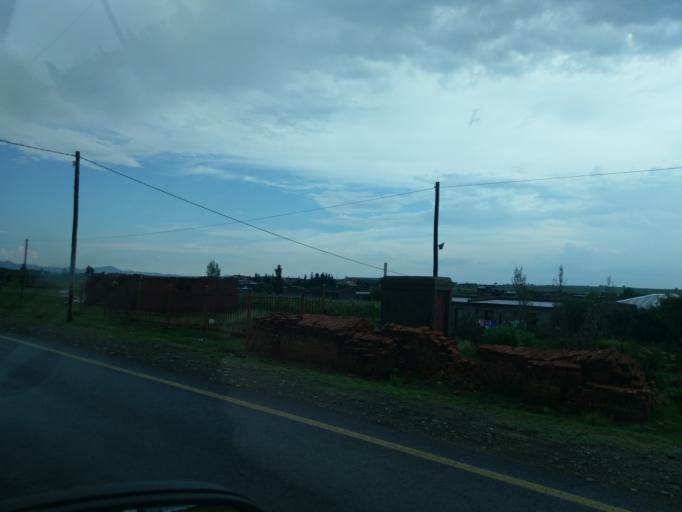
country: LS
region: Mafeteng
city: Mafeteng
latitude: -29.8001
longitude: 27.2118
